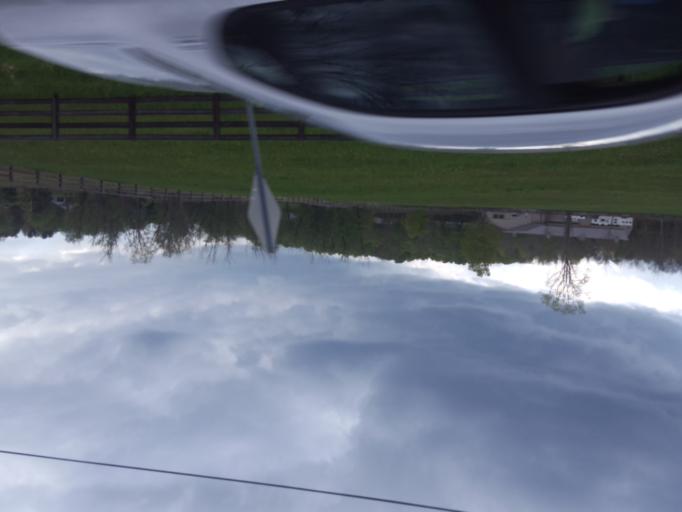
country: US
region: Ohio
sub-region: Richland County
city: Ontario
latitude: 40.7469
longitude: -82.5683
